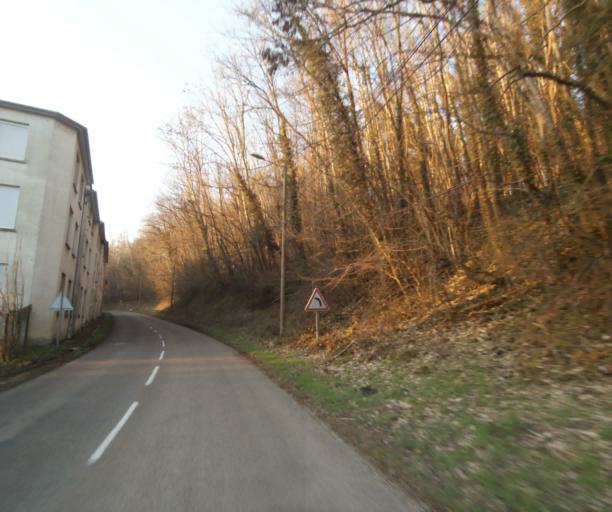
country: FR
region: Champagne-Ardenne
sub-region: Departement de la Haute-Marne
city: Bienville
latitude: 48.6111
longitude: 5.0500
